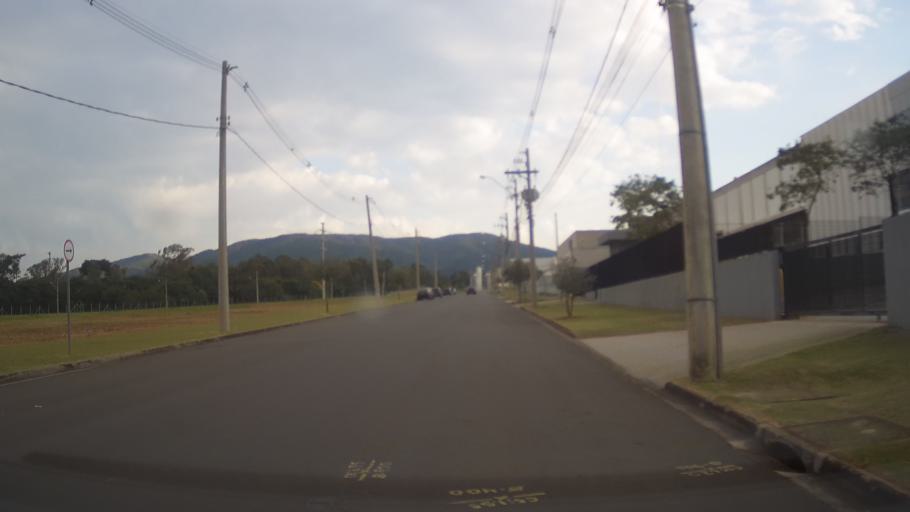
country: BR
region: Sao Paulo
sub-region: Jundiai
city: Jundiai
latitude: -23.1882
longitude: -46.9744
